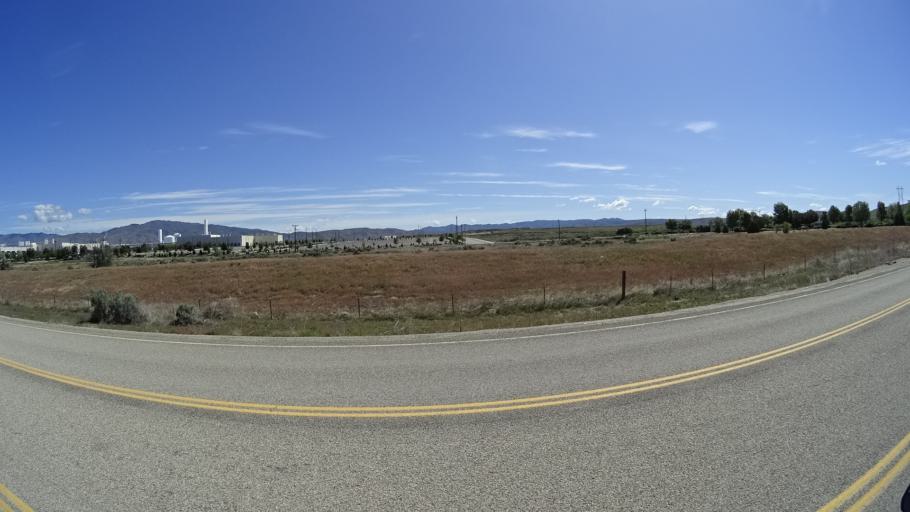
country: US
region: Idaho
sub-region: Ada County
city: Boise
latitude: 43.5192
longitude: -116.1462
